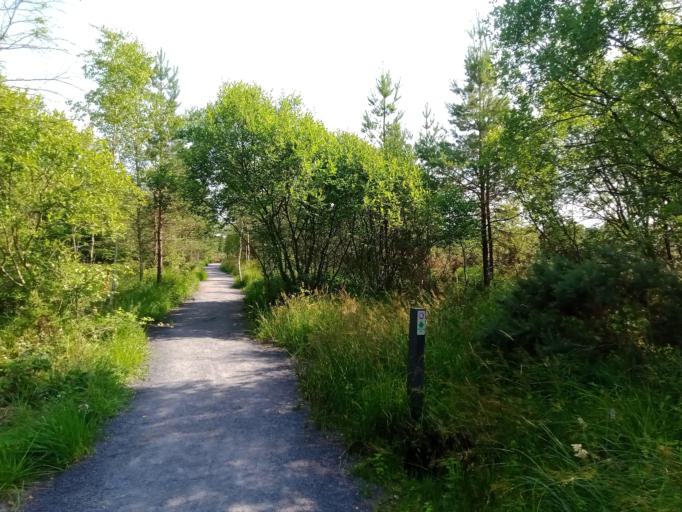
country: IE
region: Leinster
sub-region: Laois
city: Abbeyleix
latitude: 52.8987
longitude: -7.3553
